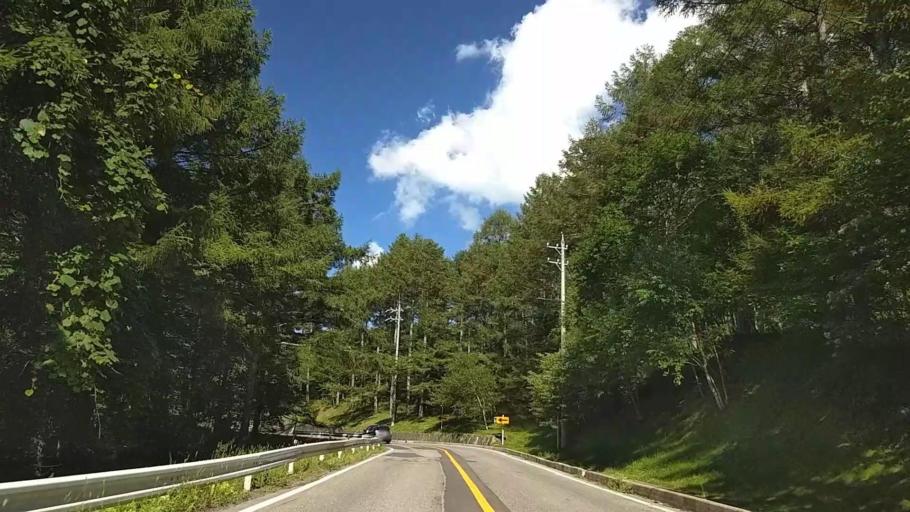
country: JP
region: Nagano
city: Chino
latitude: 36.1113
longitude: 138.2560
